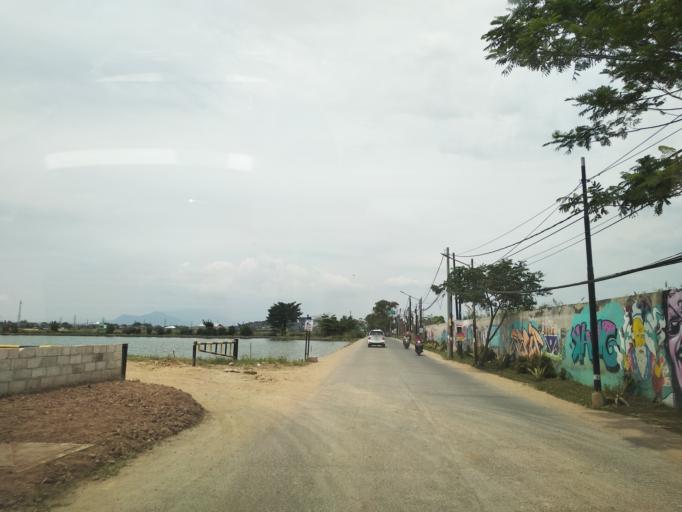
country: ID
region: West Java
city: Pameungpeuk
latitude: -6.9706
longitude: 107.6407
